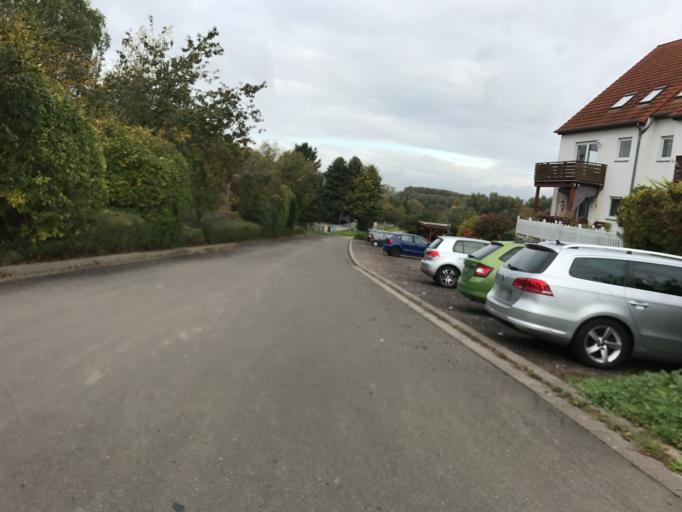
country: DE
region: Rheinland-Pfalz
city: Schwabenheim
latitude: 49.9277
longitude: 8.0908
